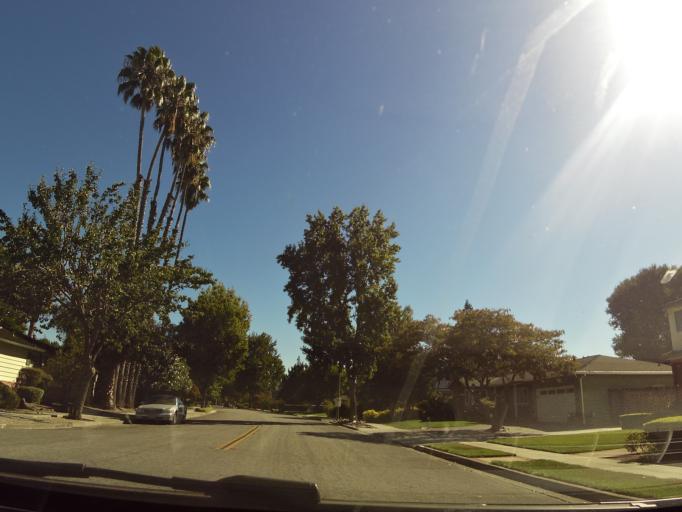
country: US
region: California
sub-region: Santa Clara County
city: Campbell
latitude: 37.2903
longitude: -121.9204
